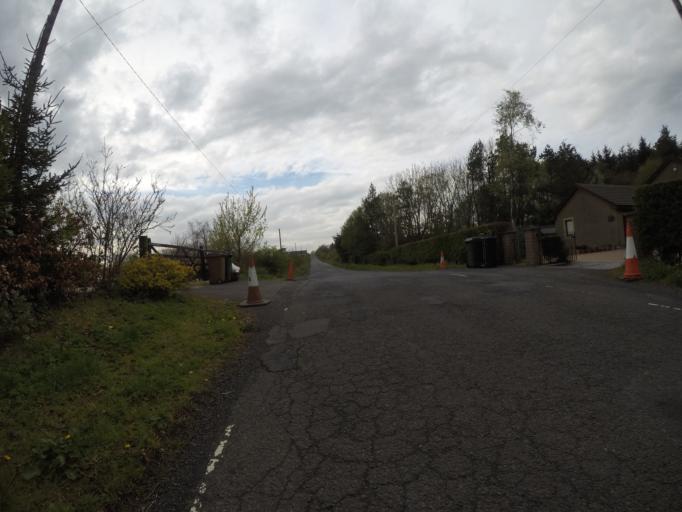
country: GB
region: Scotland
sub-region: East Ayrshire
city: Kilmarnock
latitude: 55.6411
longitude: -4.4767
